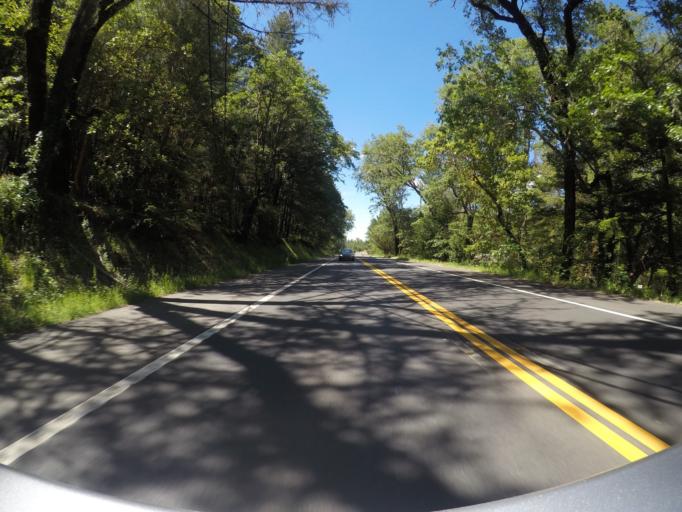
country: US
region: California
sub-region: Mendocino County
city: Laytonville
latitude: 39.6451
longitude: -123.4750
